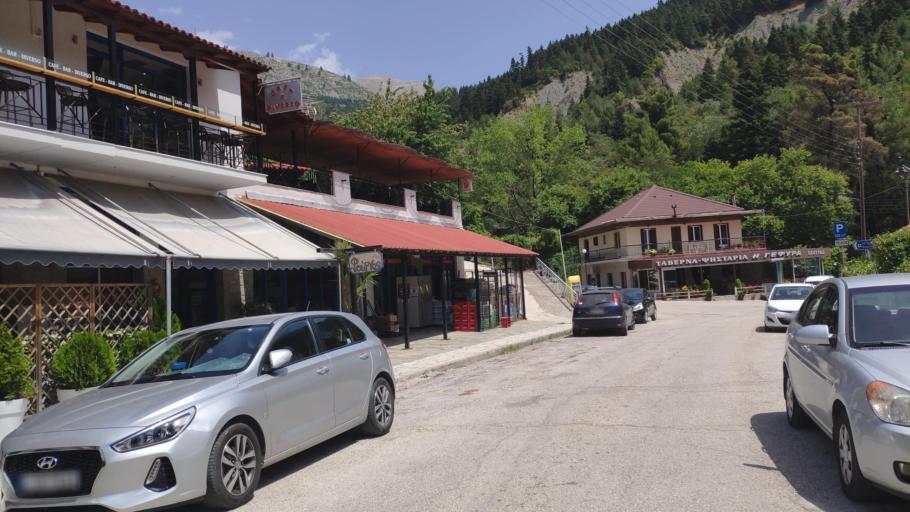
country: GR
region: Epirus
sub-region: Nomos Artas
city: Voulgareli
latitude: 39.3715
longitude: 21.1844
